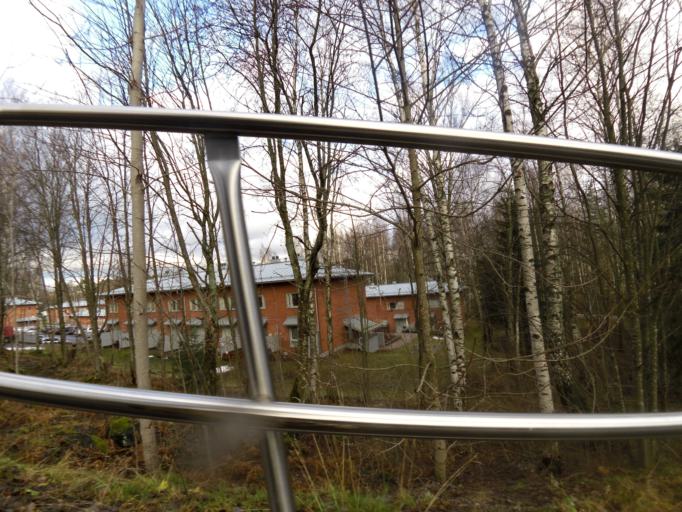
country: FI
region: Uusimaa
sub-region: Helsinki
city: Kilo
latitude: 60.1969
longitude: 24.7710
